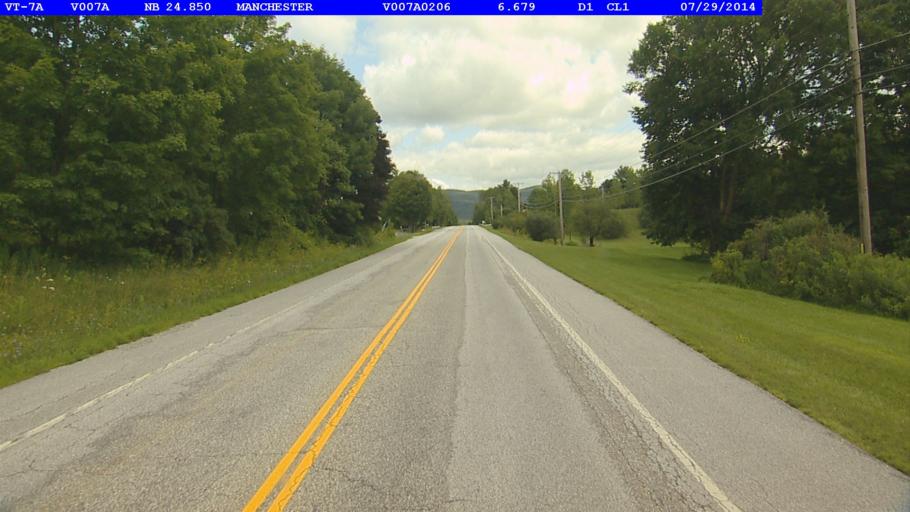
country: US
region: Vermont
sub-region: Bennington County
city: Manchester Center
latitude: 43.1958
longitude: -73.0363
